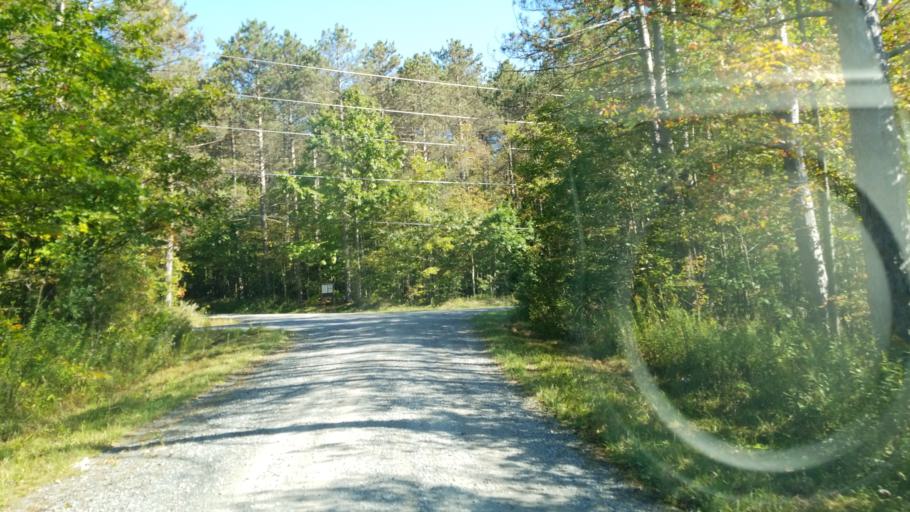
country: US
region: Pennsylvania
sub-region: Clearfield County
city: Treasure Lake
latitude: 41.1476
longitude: -78.5725
